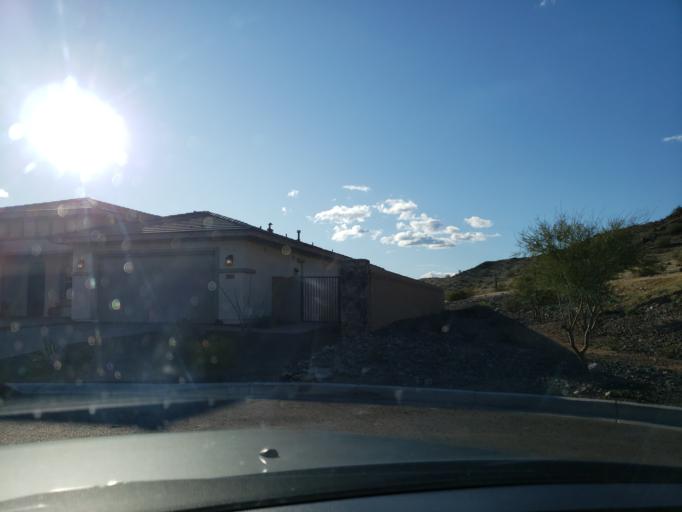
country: US
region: Arizona
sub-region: Maricopa County
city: Laveen
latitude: 33.3022
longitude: -112.1338
